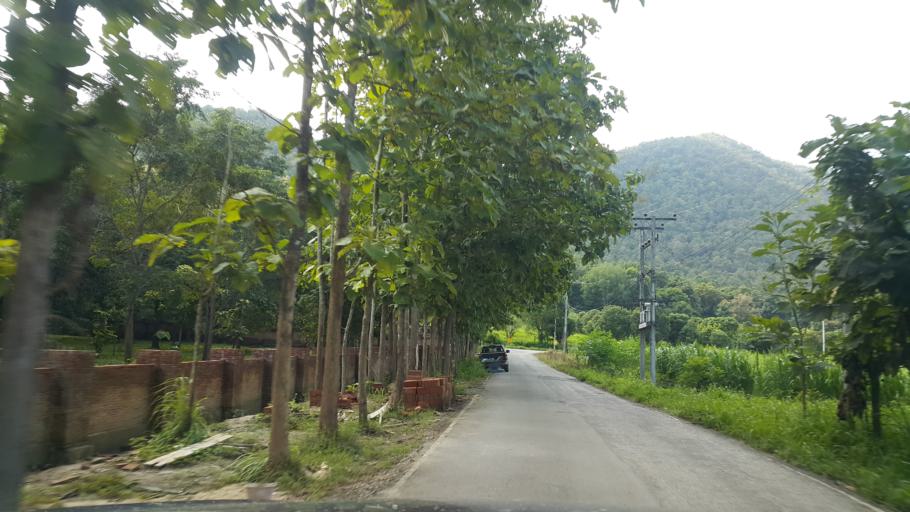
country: TH
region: Chiang Mai
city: Mae On
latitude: 18.7196
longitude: 99.2265
